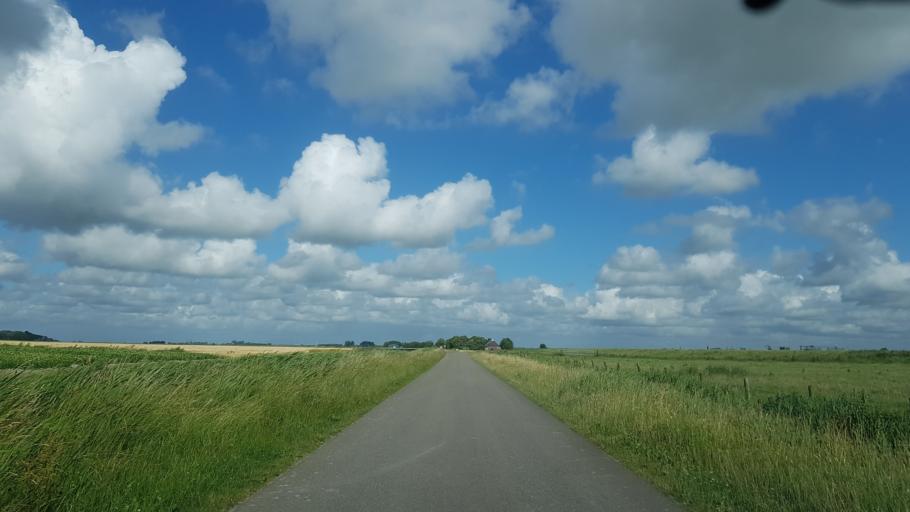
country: NL
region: Groningen
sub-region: Gemeente Winsum
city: Winsum
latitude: 53.4061
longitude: 6.5397
